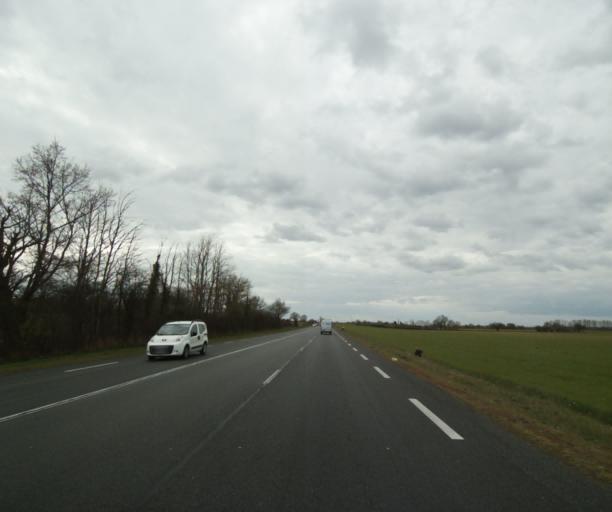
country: FR
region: Auvergne
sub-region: Departement de l'Allier
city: Toulon-sur-Allier
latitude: 46.4835
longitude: 3.3659
